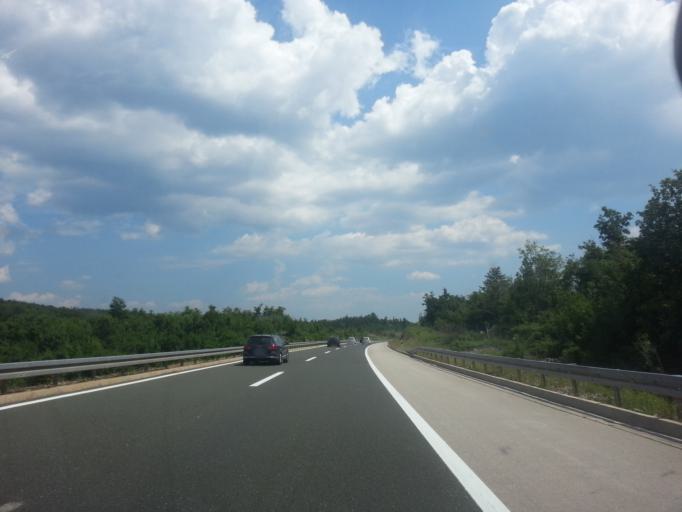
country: HR
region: Primorsko-Goranska
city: Matulji
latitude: 45.4271
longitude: 14.2946
